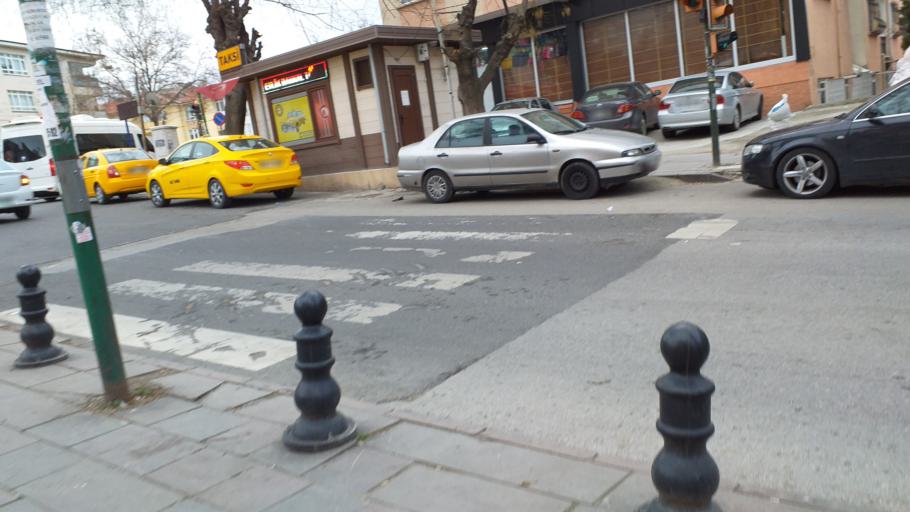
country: TR
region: Ankara
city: Ankara
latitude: 39.9799
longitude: 32.8364
